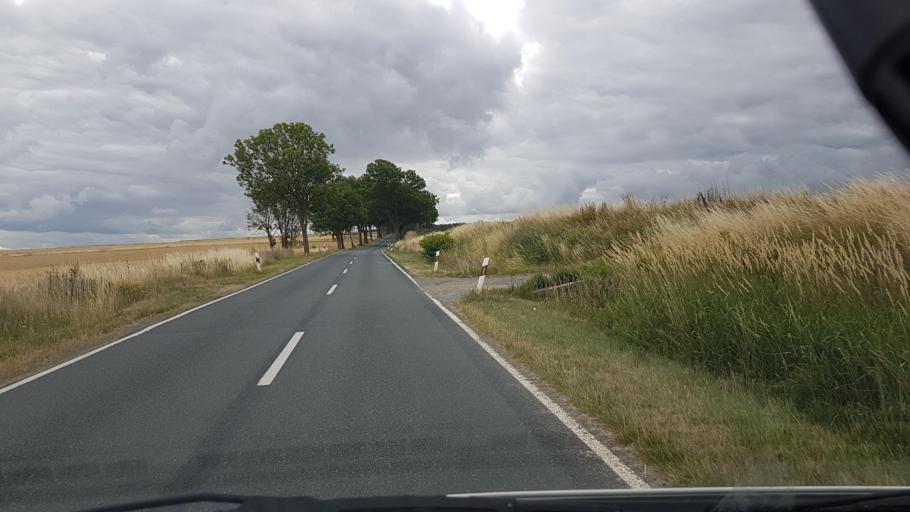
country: DE
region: Lower Saxony
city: Rabke
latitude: 52.1907
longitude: 10.8841
